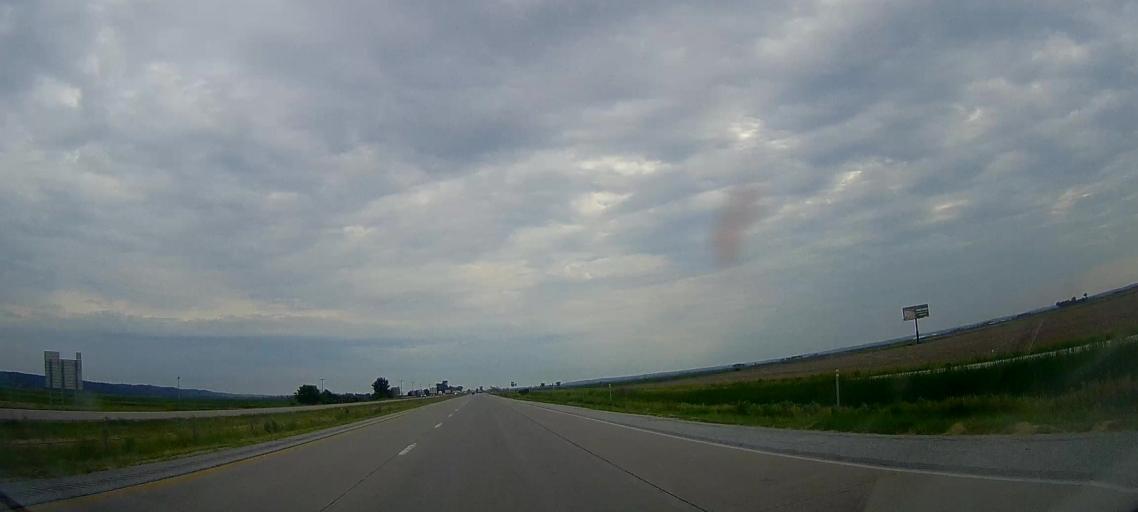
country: US
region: Iowa
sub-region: Harrison County
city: Missouri Valley
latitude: 41.5456
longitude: -95.9177
